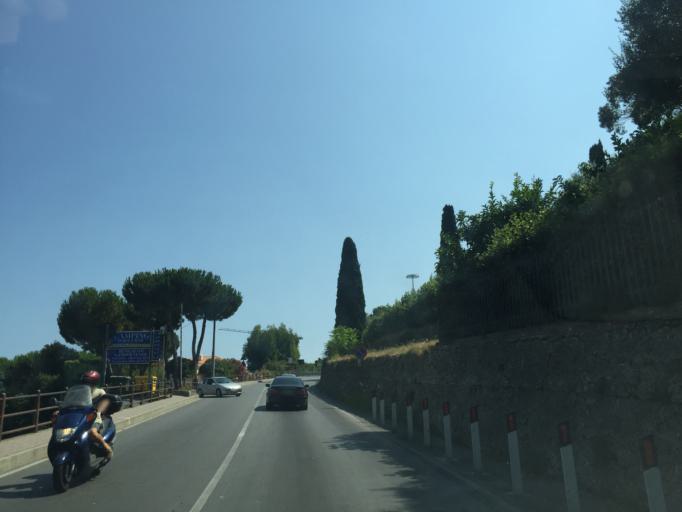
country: IT
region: Liguria
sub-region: Provincia di Imperia
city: Ventimiglia
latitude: 43.7941
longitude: 7.5631
